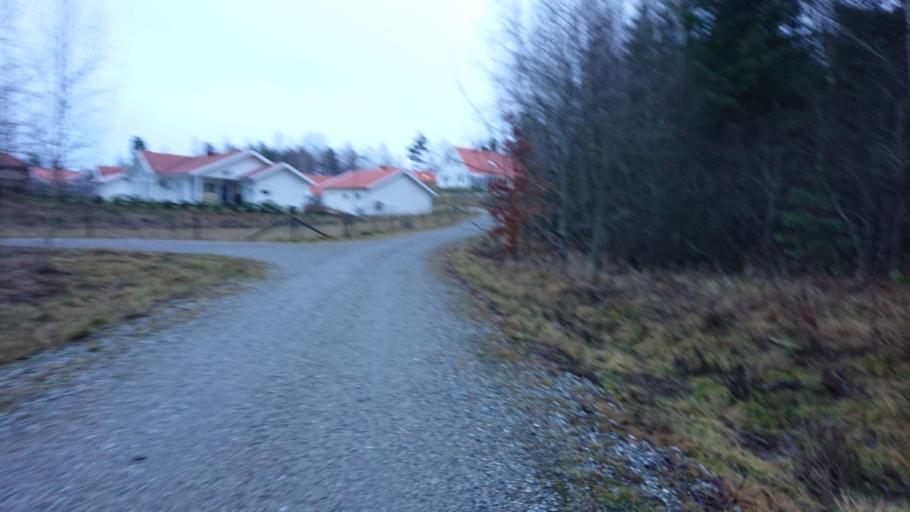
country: SE
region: Soedermanland
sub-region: Strangnas Kommun
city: Stallarholmen
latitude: 59.3662
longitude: 17.1835
